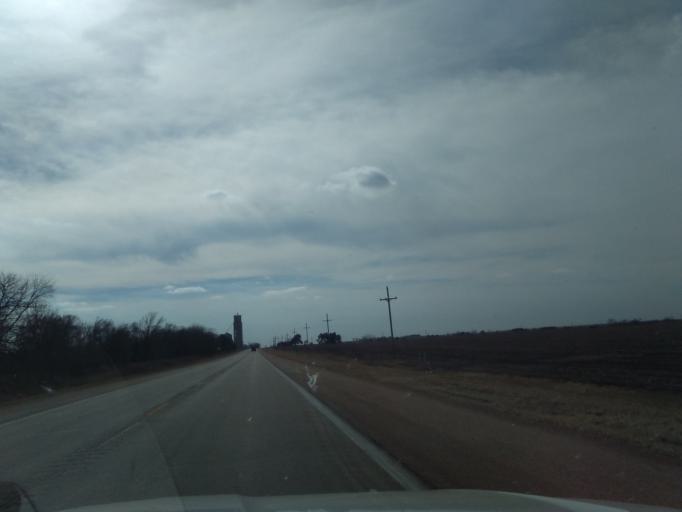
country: US
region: Nebraska
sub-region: Jefferson County
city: Fairbury
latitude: 40.1968
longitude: -96.9655
